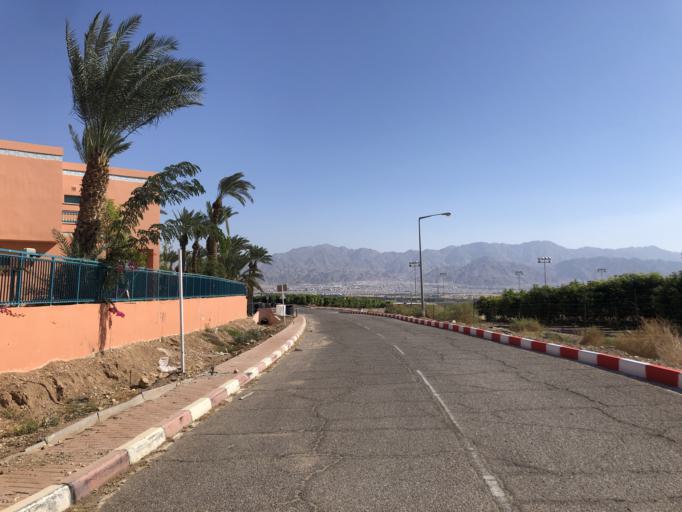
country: IL
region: Southern District
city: Eilat
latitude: 29.5798
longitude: 34.9609
